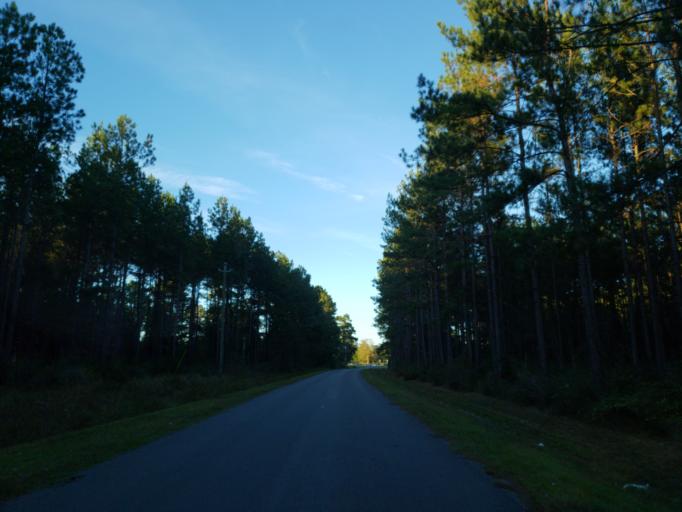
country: US
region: Mississippi
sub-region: Wayne County
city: Belmont
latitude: 31.4566
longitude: -88.5226
